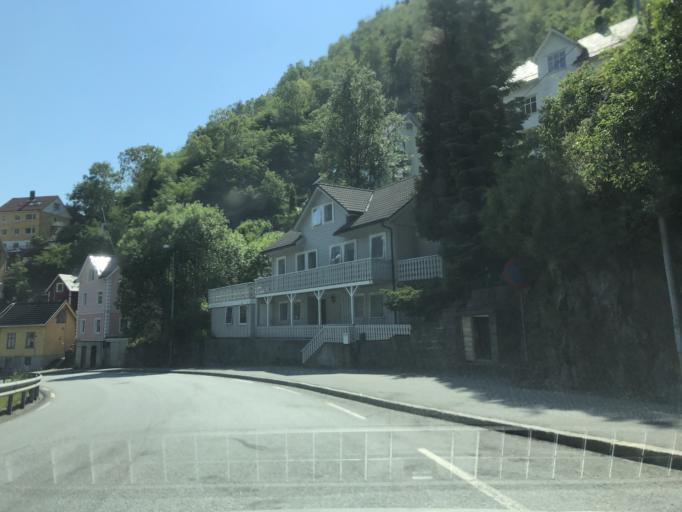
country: NO
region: Hordaland
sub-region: Odda
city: Odda
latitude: 60.0719
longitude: 6.5394
